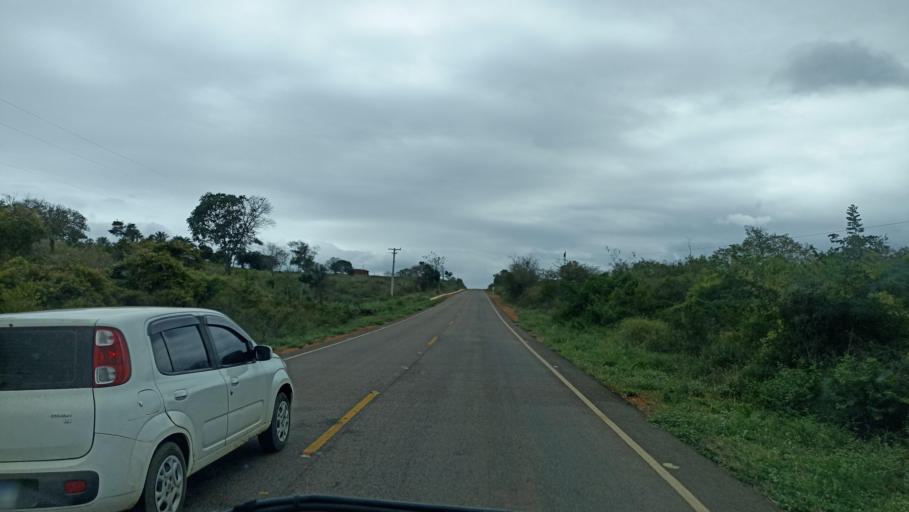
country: BR
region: Bahia
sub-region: Andarai
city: Vera Cruz
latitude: -12.9942
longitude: -40.9983
